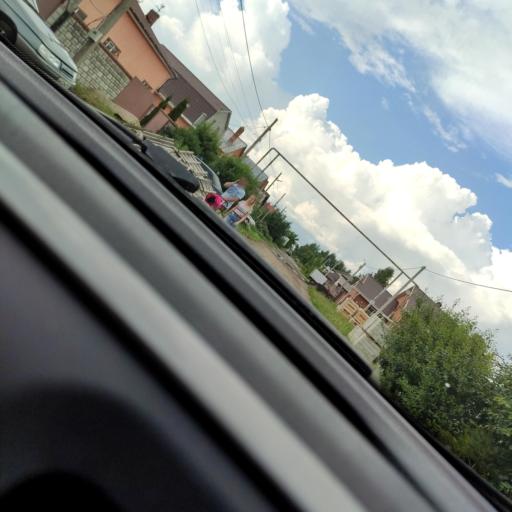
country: RU
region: Samara
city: Tol'yatti
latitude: 53.5561
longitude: 49.4069
